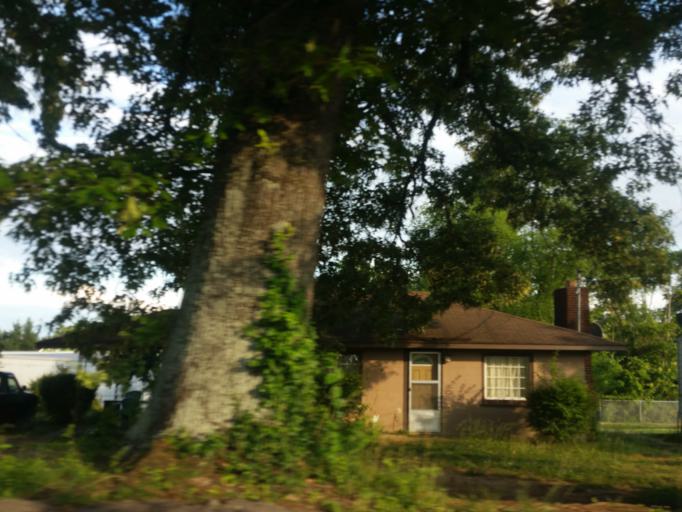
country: US
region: Tennessee
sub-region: Knox County
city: Knoxville
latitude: 35.9957
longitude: -83.9065
